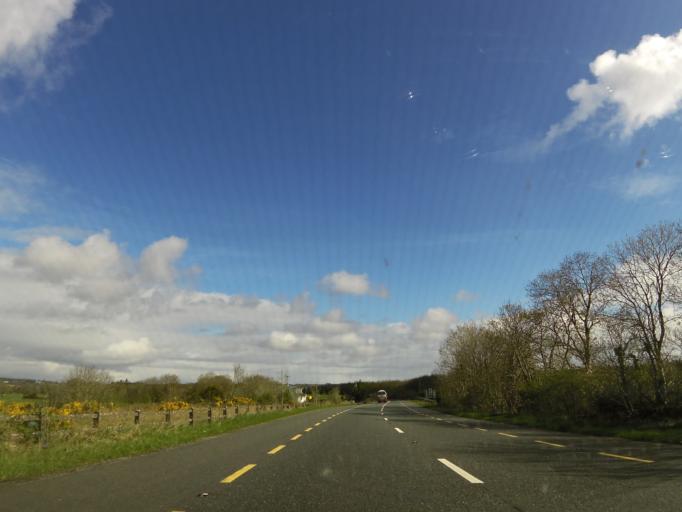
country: IE
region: Connaught
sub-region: Maigh Eo
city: Ballyhaunis
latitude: 53.8555
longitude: -8.8563
